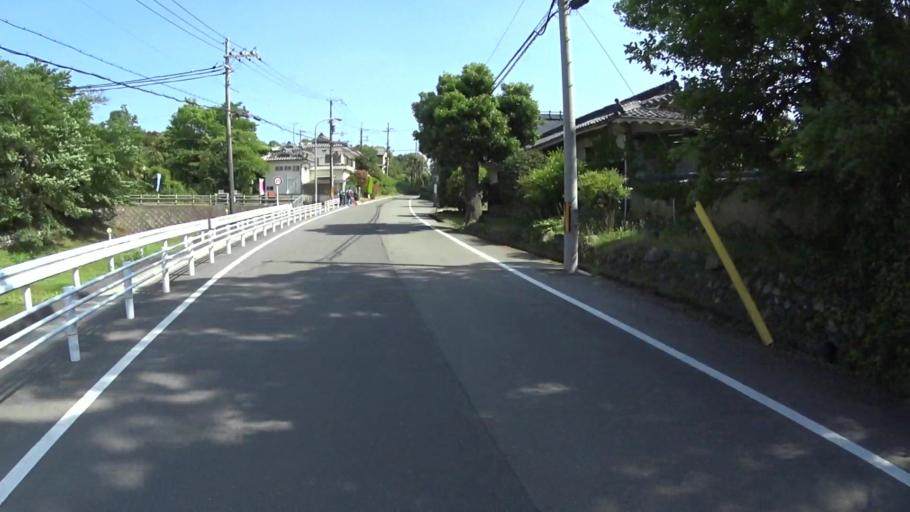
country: JP
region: Kyoto
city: Kameoka
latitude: 35.0353
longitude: 135.5859
